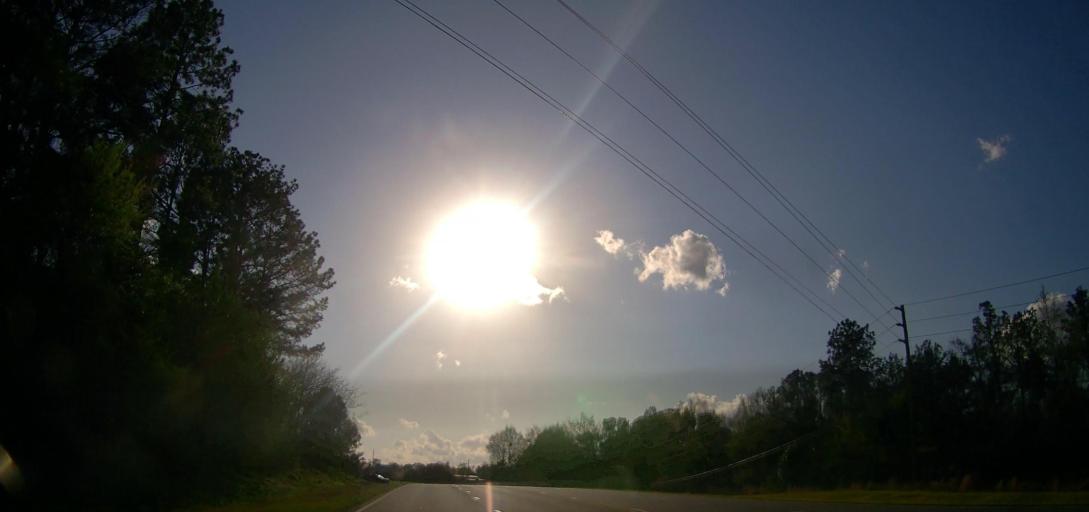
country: US
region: Georgia
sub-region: Baldwin County
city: Milledgeville
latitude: 33.0911
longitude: -83.2445
